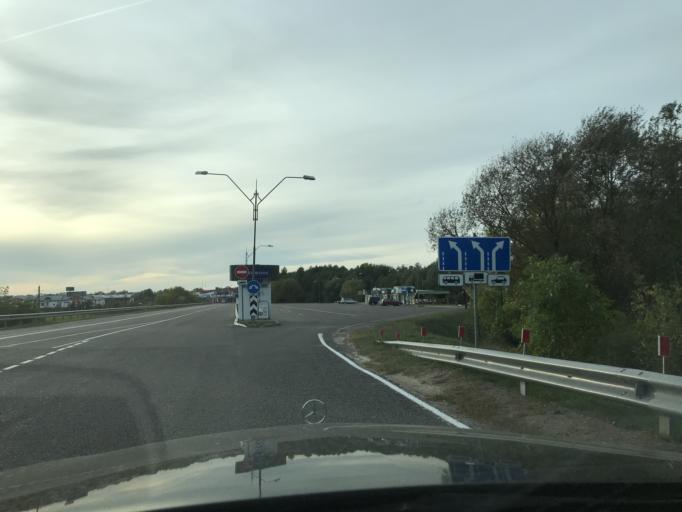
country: PL
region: Lublin Voivodeship
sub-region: Powiat bialski
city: Slawatycze
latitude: 51.7614
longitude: 23.6083
